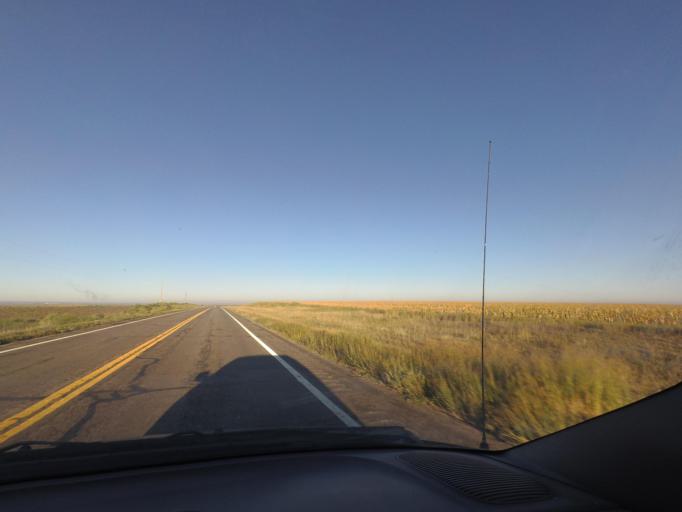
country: US
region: Colorado
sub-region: Washington County
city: Akron
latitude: 39.6992
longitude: -103.0523
